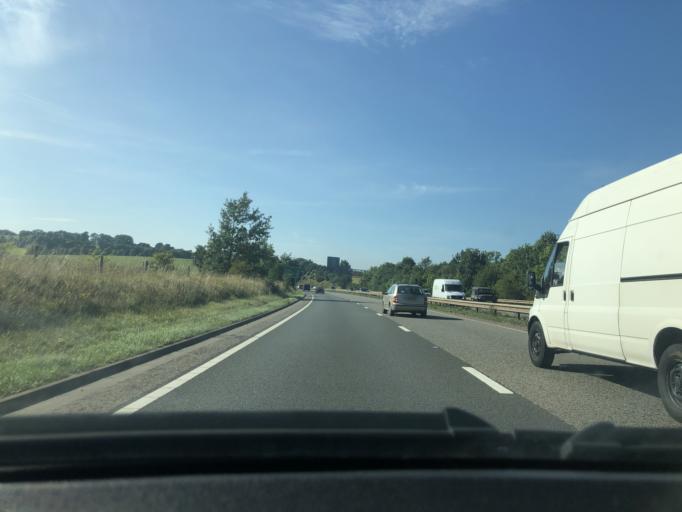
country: GB
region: England
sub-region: Devon
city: Exminster
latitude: 50.6844
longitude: -3.5218
